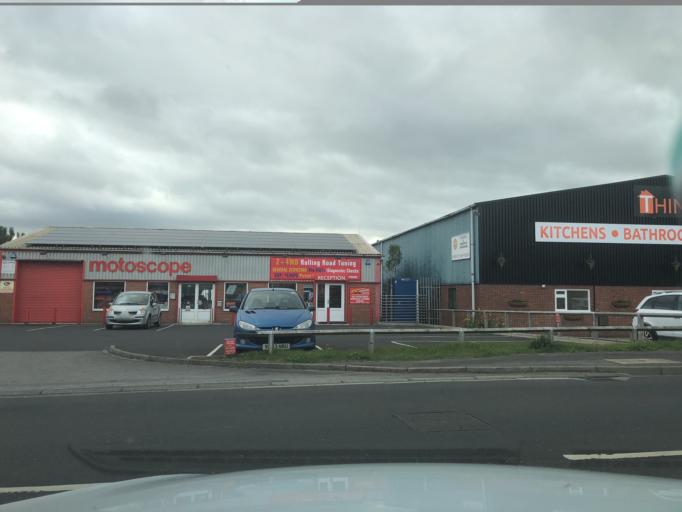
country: GB
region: England
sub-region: North Yorkshire
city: Northallerton
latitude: 54.3473
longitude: -1.4479
